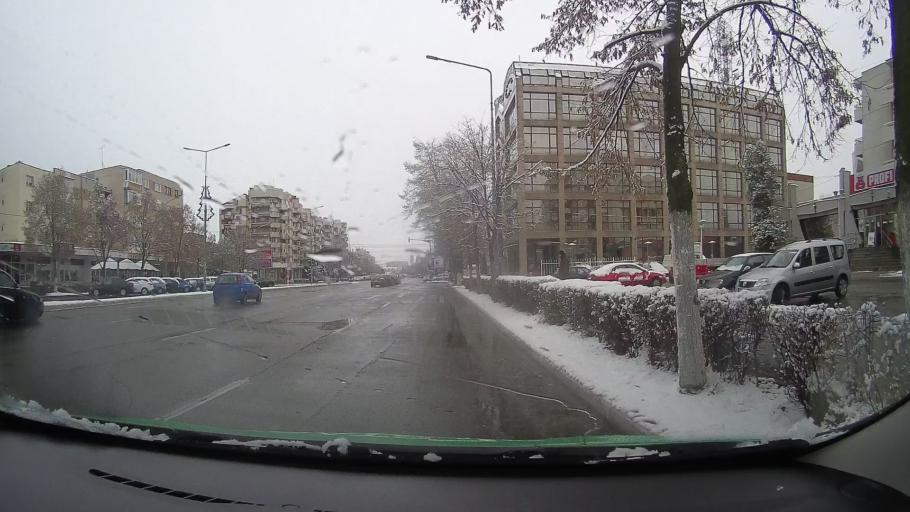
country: RO
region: Hunedoara
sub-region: Municipiul Deva
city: Deva
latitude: 45.8726
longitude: 22.9091
